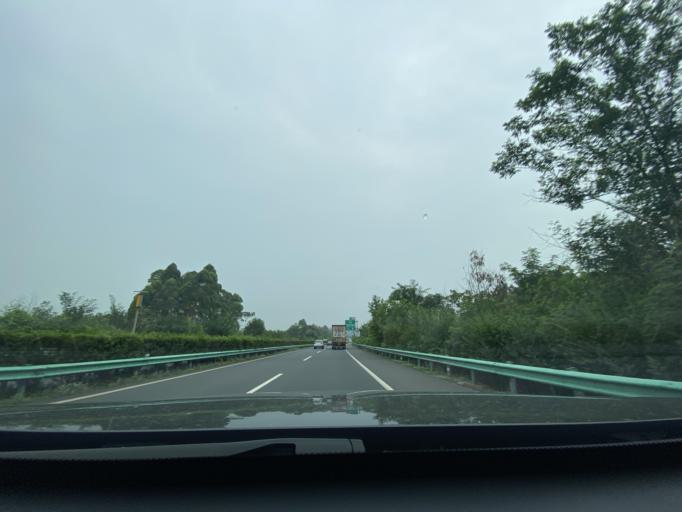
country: CN
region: Sichuan
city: Longquan
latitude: 30.3098
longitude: 104.1186
